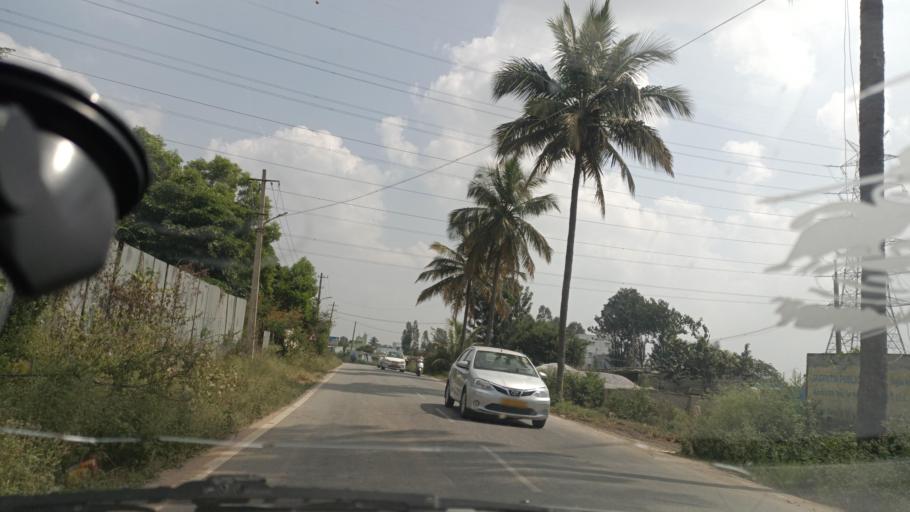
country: IN
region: Karnataka
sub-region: Bangalore Rural
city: Devanhalli
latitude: 13.1787
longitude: 77.6485
